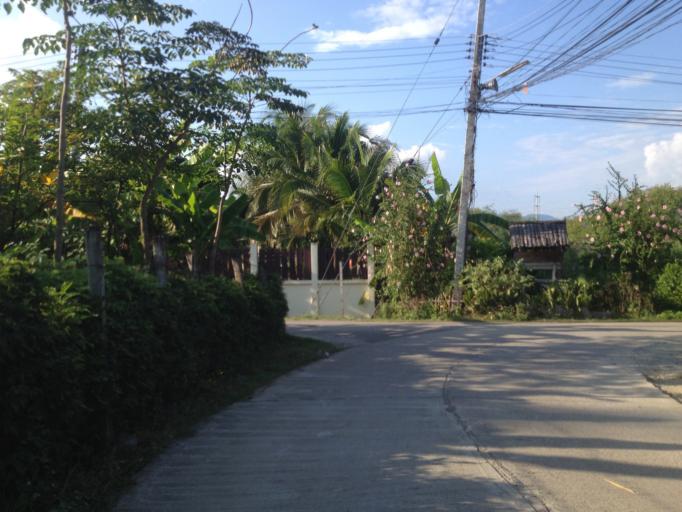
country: TH
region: Chiang Mai
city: Hang Dong
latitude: 18.7216
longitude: 98.9394
